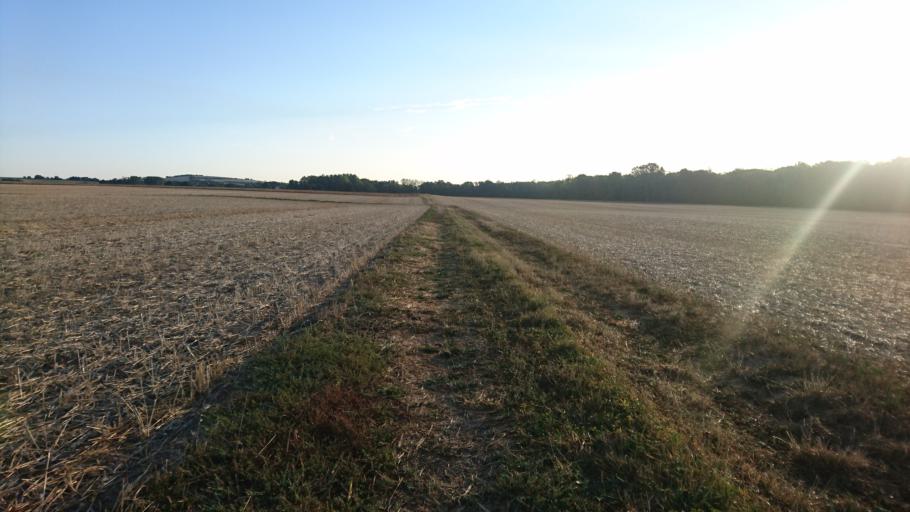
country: FR
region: Bourgogne
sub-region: Departement de l'Yonne
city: Fleury-la-Vallee
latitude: 47.8728
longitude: 3.4017
